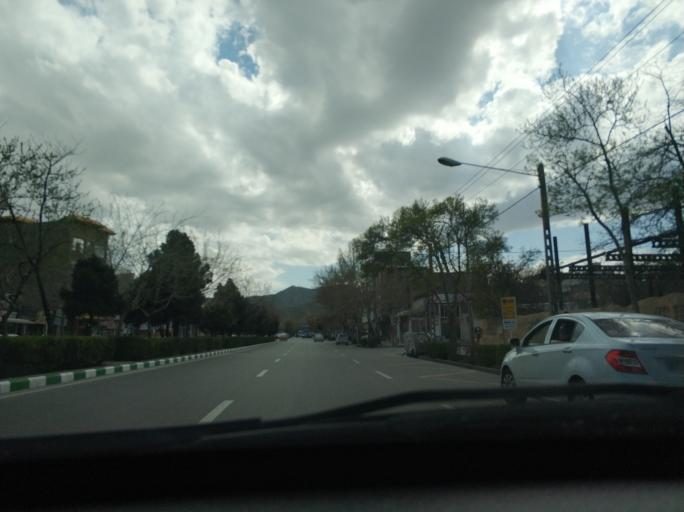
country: IR
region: Razavi Khorasan
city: Mashhad
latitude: 36.2687
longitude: 59.5880
